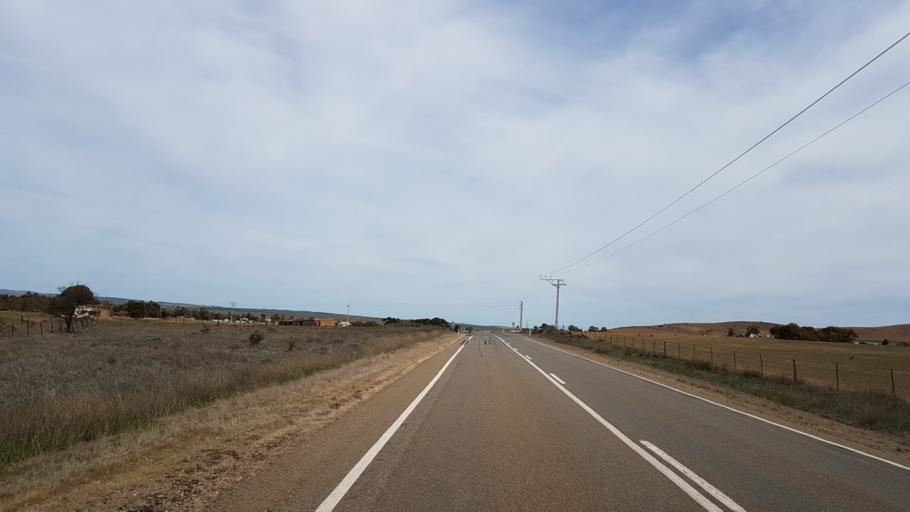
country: AU
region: South Australia
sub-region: Peterborough
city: Peterborough
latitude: -33.0207
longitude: 138.7523
